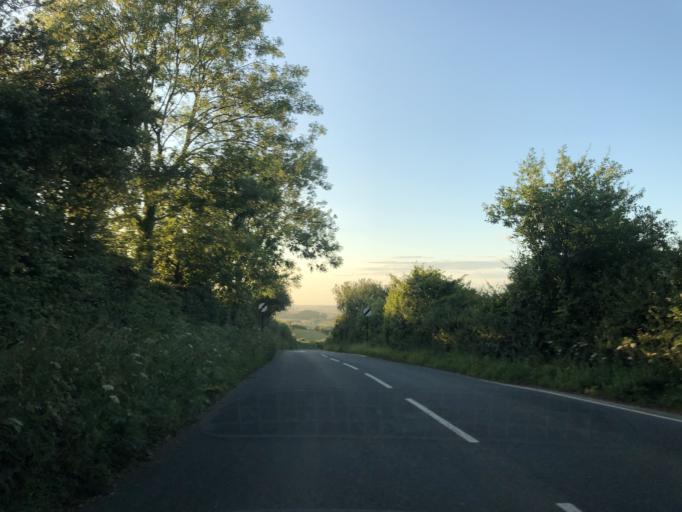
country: GB
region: England
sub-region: Isle of Wight
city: Niton
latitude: 50.6022
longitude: -1.2791
